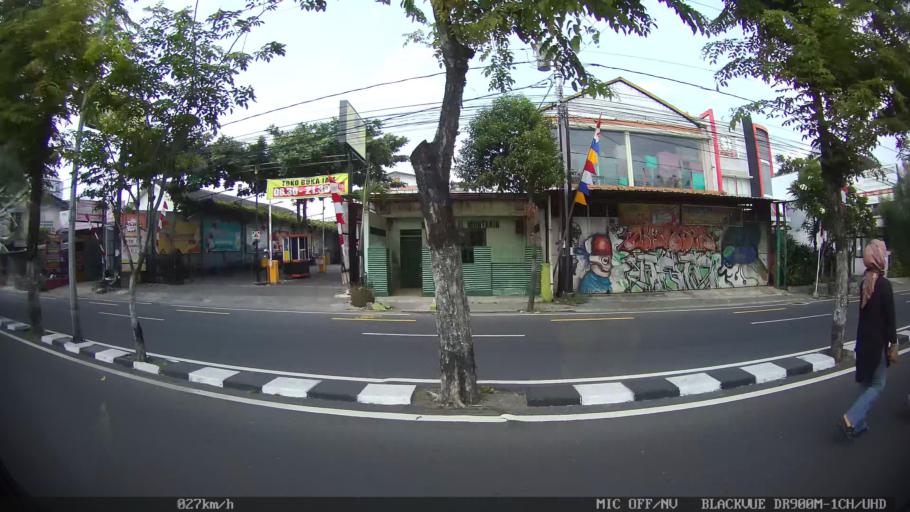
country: ID
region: Daerah Istimewa Yogyakarta
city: Yogyakarta
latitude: -7.8166
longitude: 110.3793
